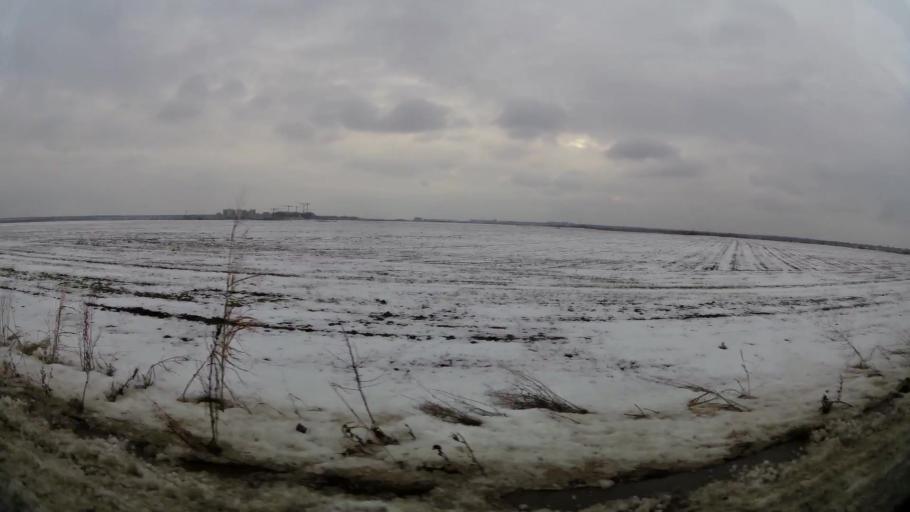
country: RO
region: Ilfov
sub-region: Comuna Tunari
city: Tunari
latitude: 44.5524
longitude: 26.1733
